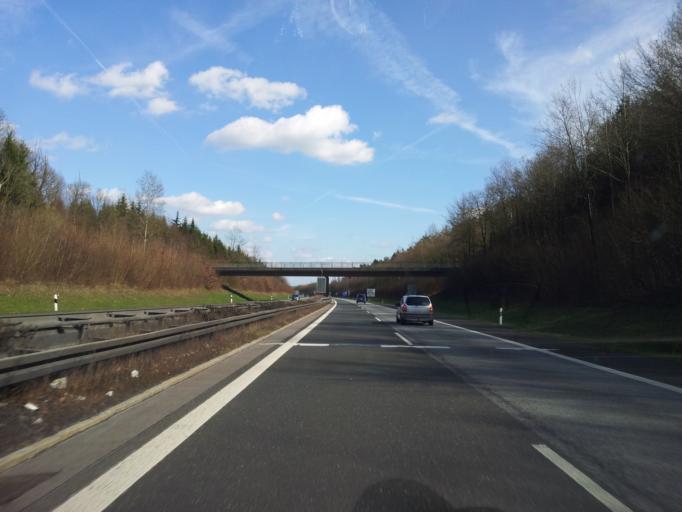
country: DE
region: Bavaria
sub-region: Regierungsbezirk Unterfranken
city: Donnersdorf
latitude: 50.0031
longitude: 10.4025
